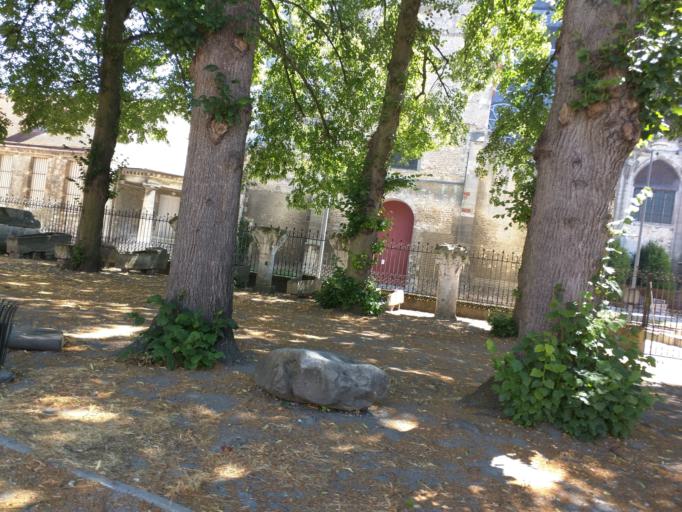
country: FR
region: Picardie
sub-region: Departement de l'Oise
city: Beauvais
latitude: 49.4329
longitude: 2.0802
